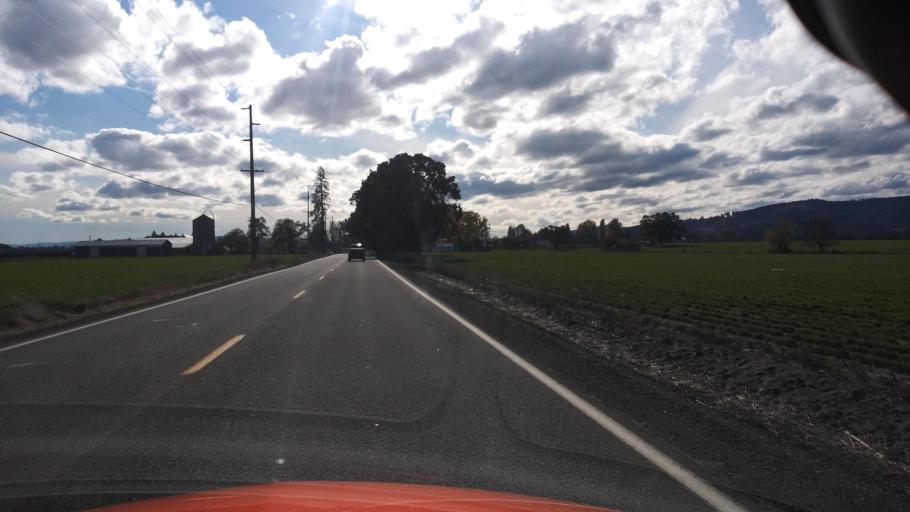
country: US
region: Oregon
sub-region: Washington County
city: Banks
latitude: 45.5898
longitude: -123.1144
